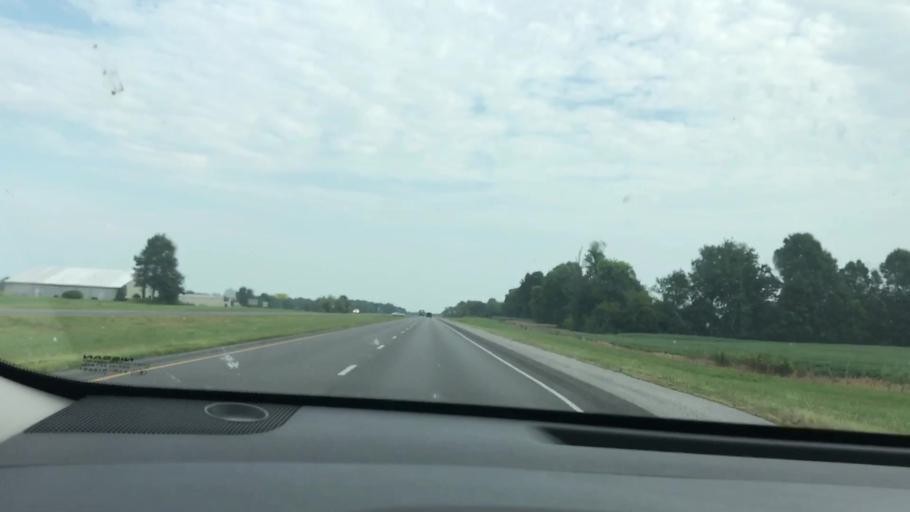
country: US
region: Kentucky
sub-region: Calloway County
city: Murray
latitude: 36.6889
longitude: -88.3029
